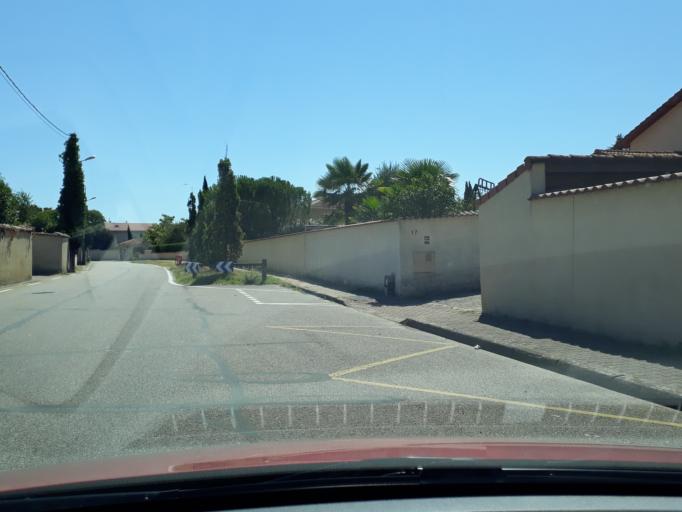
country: FR
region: Rhone-Alpes
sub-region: Departement du Rhone
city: Genas
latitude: 45.7006
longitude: 4.9818
